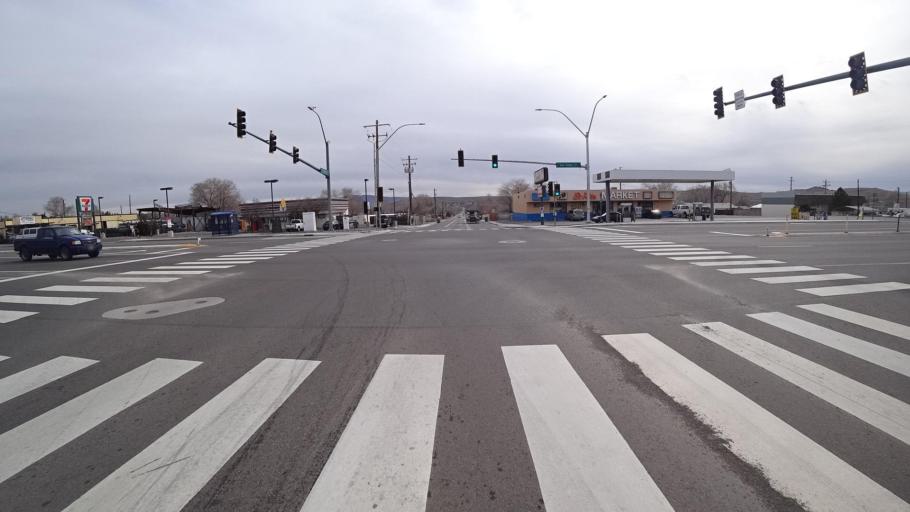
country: US
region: Nevada
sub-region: Washoe County
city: Sun Valley
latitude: 39.6000
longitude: -119.7808
